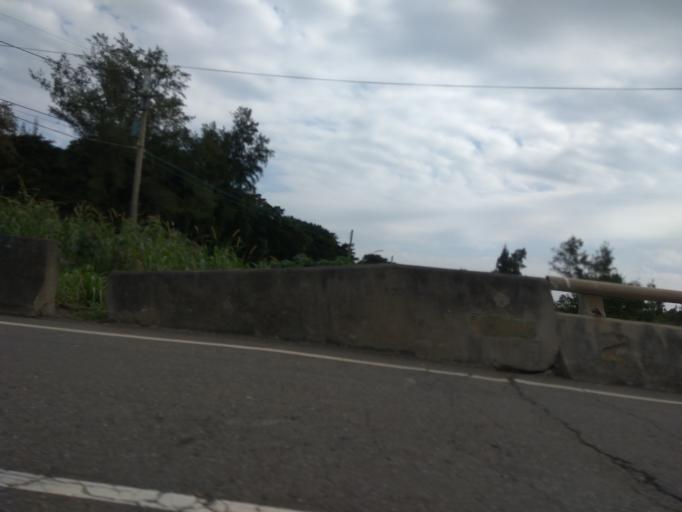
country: TW
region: Taiwan
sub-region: Hsinchu
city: Zhubei
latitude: 24.9841
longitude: 121.0271
